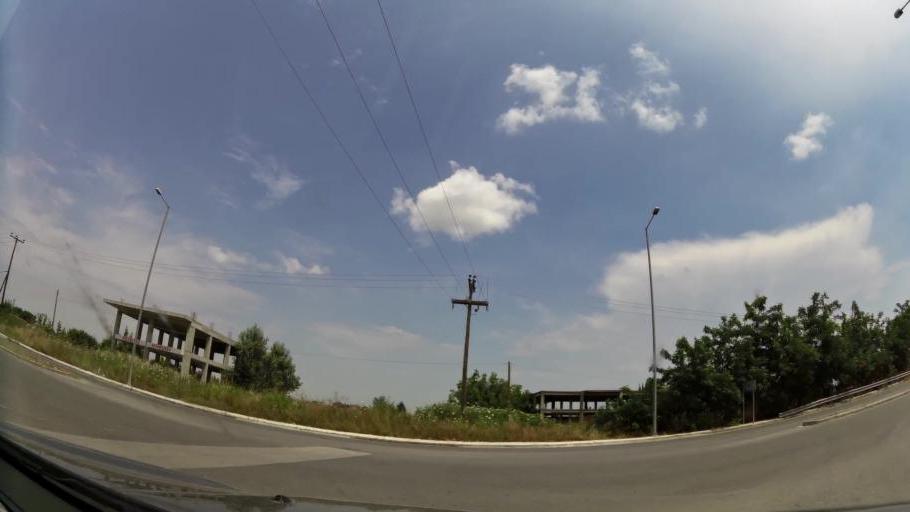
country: GR
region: Central Macedonia
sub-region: Nomos Pierias
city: Peristasi
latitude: 40.2747
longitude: 22.5328
